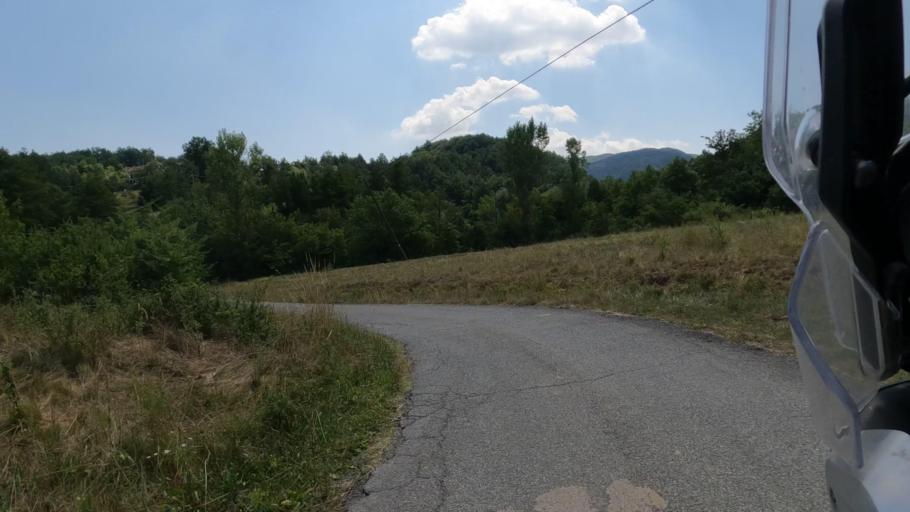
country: IT
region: Piedmont
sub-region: Provincia di Alessandria
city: Cassinelle-Concentrico
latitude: 44.5716
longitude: 8.5565
